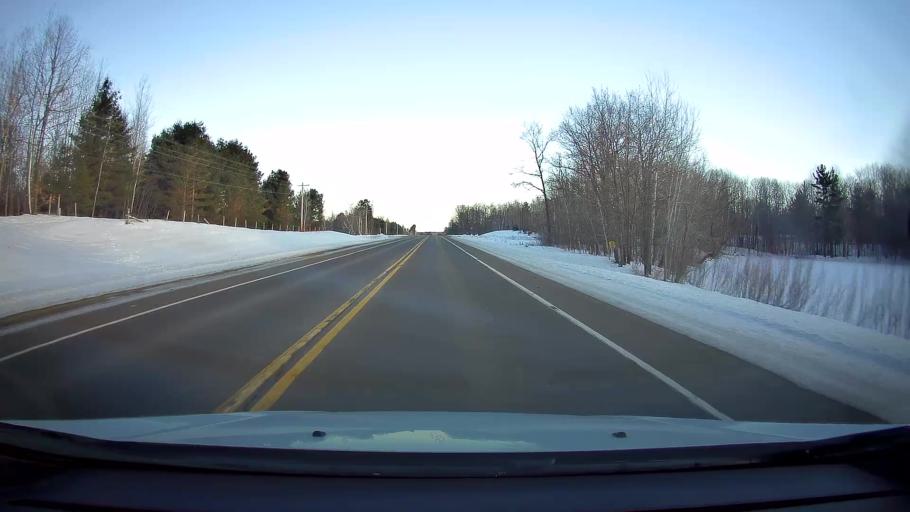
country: US
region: Wisconsin
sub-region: Barron County
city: Cumberland
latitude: 45.5874
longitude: -92.0176
